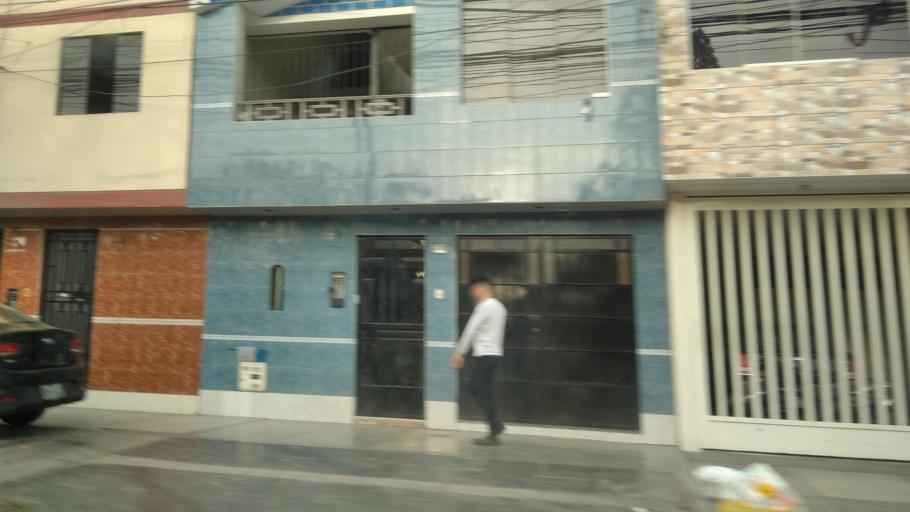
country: PE
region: Lima
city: Lima
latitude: -12.0097
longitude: -76.9993
